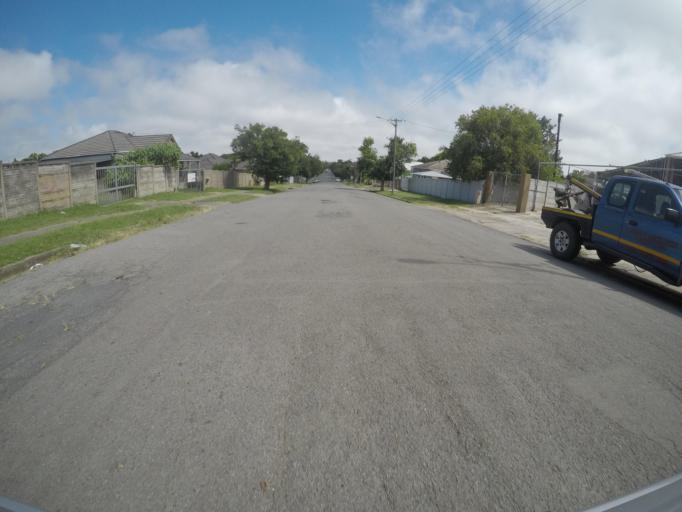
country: ZA
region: Eastern Cape
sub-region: Buffalo City Metropolitan Municipality
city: East London
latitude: -32.9754
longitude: 27.8895
